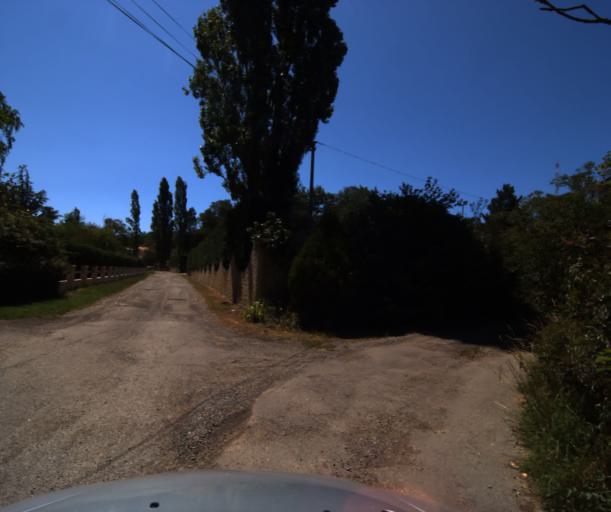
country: FR
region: Midi-Pyrenees
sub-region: Departement de la Haute-Garonne
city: Muret
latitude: 43.4534
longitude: 1.3440
